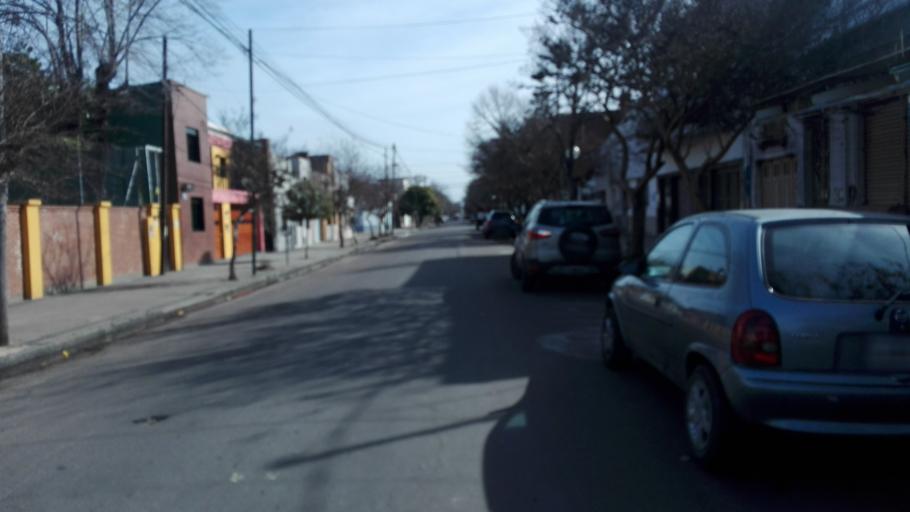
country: AR
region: Buenos Aires
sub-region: Partido de La Plata
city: La Plata
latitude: -34.9384
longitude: -57.9408
